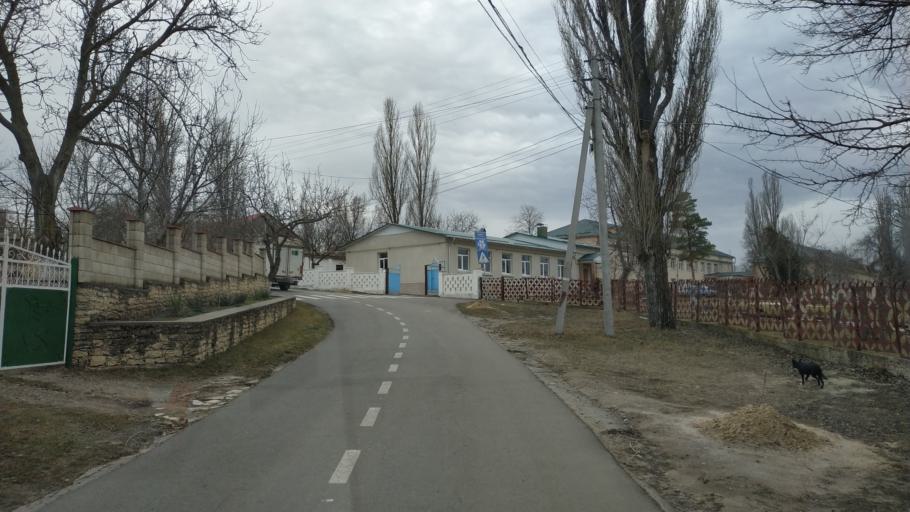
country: MD
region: Telenesti
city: Cocieri
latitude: 47.3485
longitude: 29.0910
